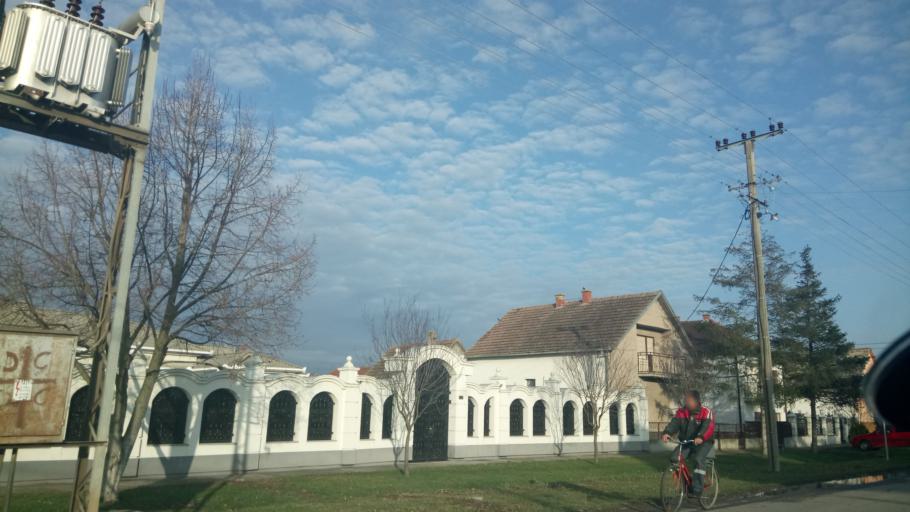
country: RS
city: Vojka
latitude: 44.9366
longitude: 20.1350
